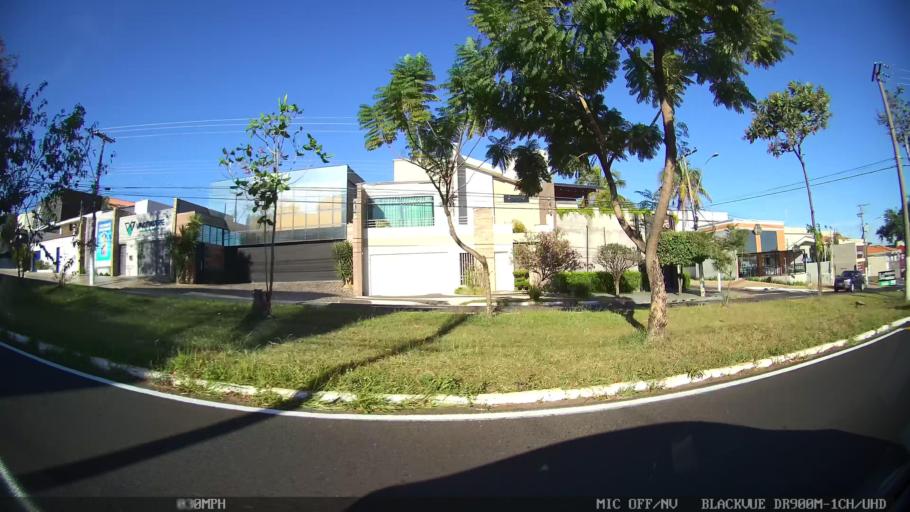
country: BR
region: Sao Paulo
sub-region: Franca
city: Franca
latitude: -20.5567
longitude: -47.4053
